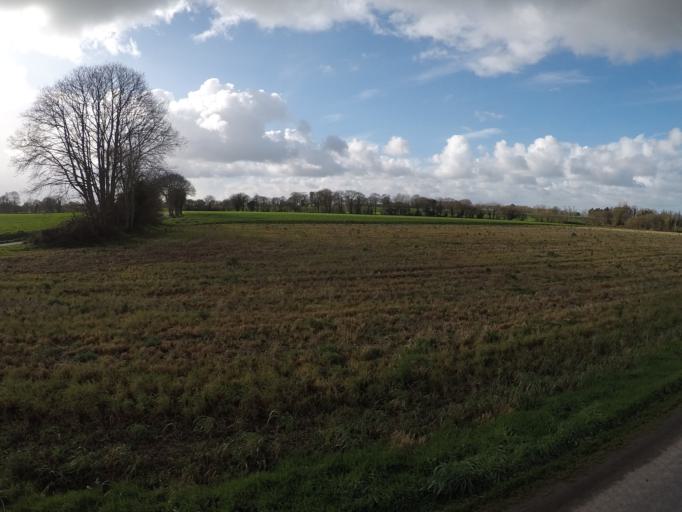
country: FR
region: Brittany
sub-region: Departement des Cotes-d'Armor
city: Goudelin
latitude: 48.6117
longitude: -2.9979
